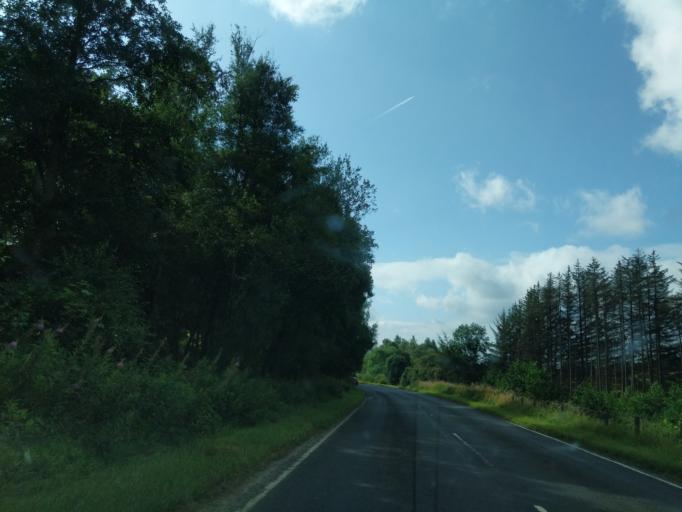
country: GB
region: Scotland
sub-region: The Scottish Borders
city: Peebles
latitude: 55.7405
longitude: -3.2060
